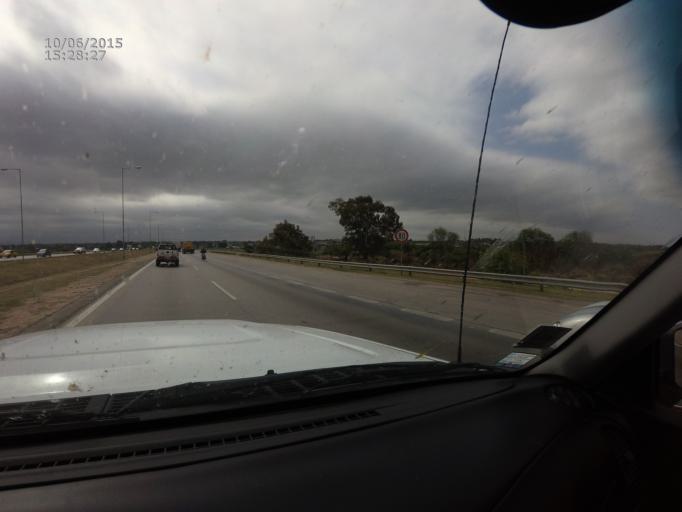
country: AR
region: Cordoba
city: Malvinas Argentinas
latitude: -31.4102
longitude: -64.1207
